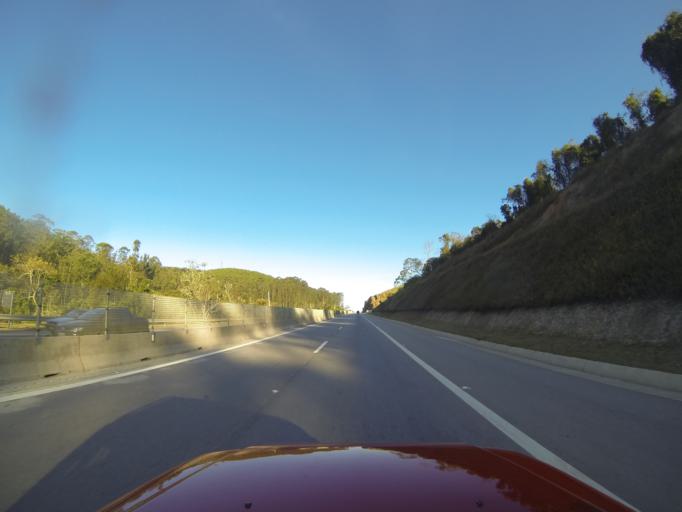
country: BR
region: Sao Paulo
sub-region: Santa Branca
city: Santa Branca
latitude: -23.2919
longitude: -45.7835
